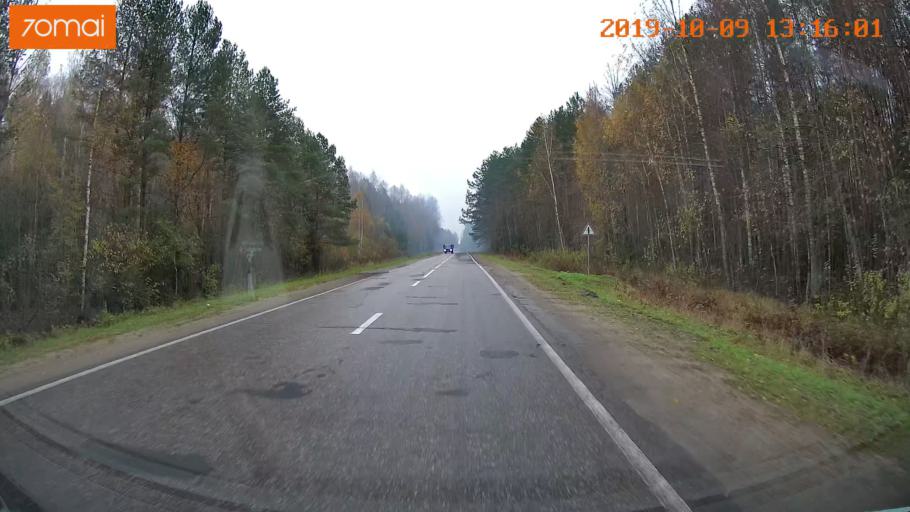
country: RU
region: Jaroslavl
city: Lyubim
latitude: 58.3640
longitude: 40.7603
